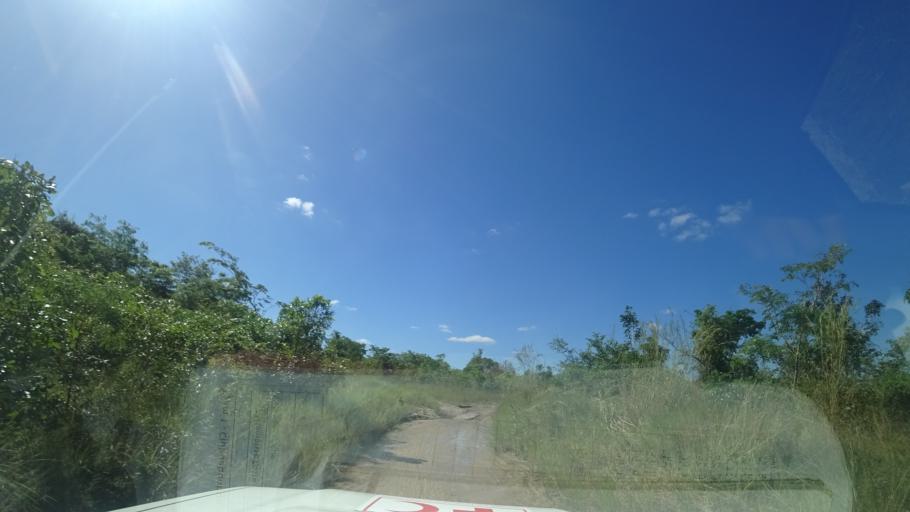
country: MZ
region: Sofala
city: Dondo
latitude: -19.4768
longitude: 34.6287
